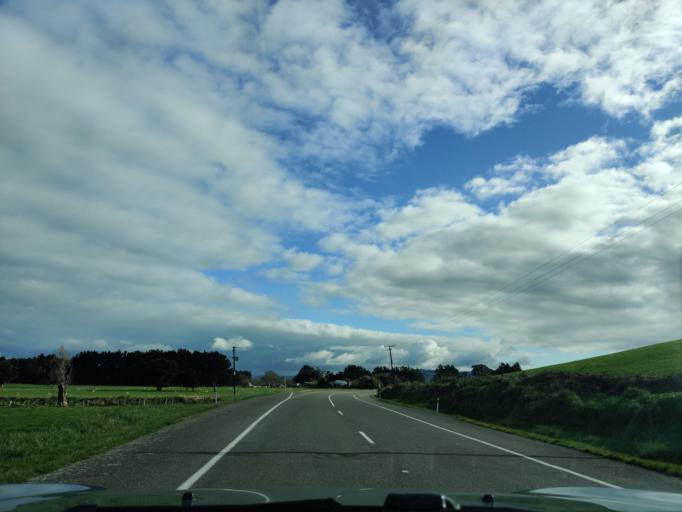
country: NZ
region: Manawatu-Wanganui
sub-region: Palmerston North City
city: Palmerston North
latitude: -40.3403
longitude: 175.8873
